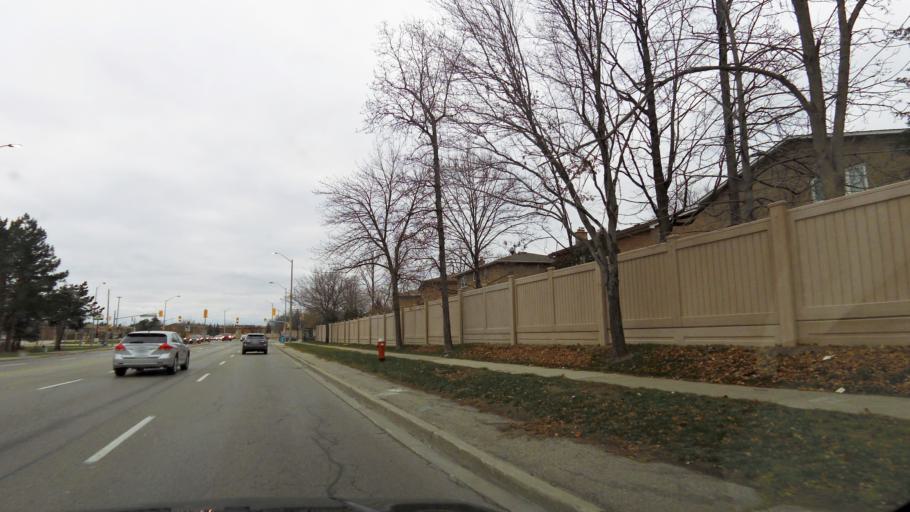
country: CA
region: Ontario
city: Mississauga
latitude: 43.5697
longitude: -79.6674
